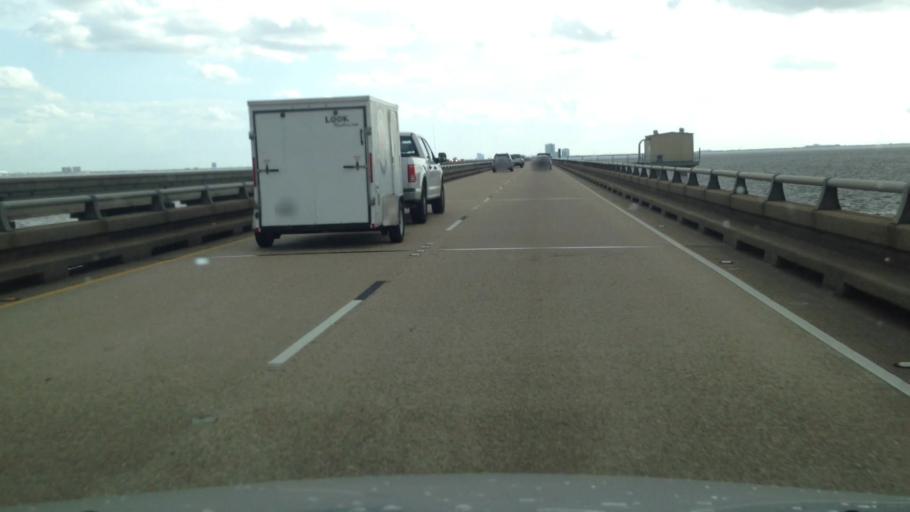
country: US
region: Louisiana
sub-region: Jefferson Parish
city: Metairie
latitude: 30.0907
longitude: -90.1421
